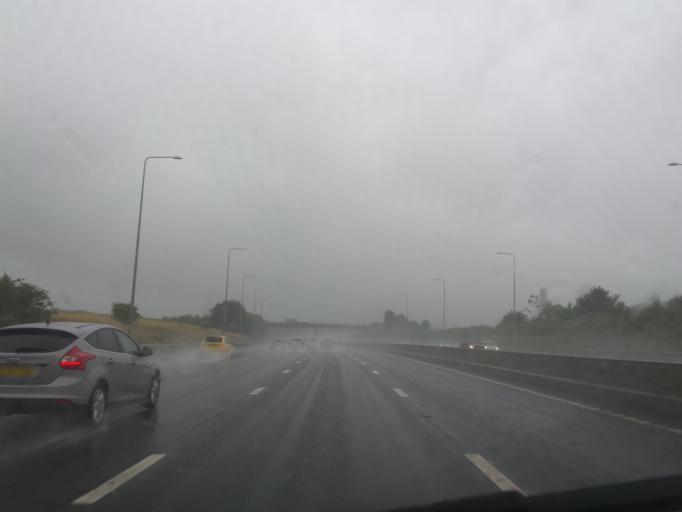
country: GB
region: England
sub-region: Nottinghamshire
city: Kimberley
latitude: 53.0105
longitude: -1.2397
